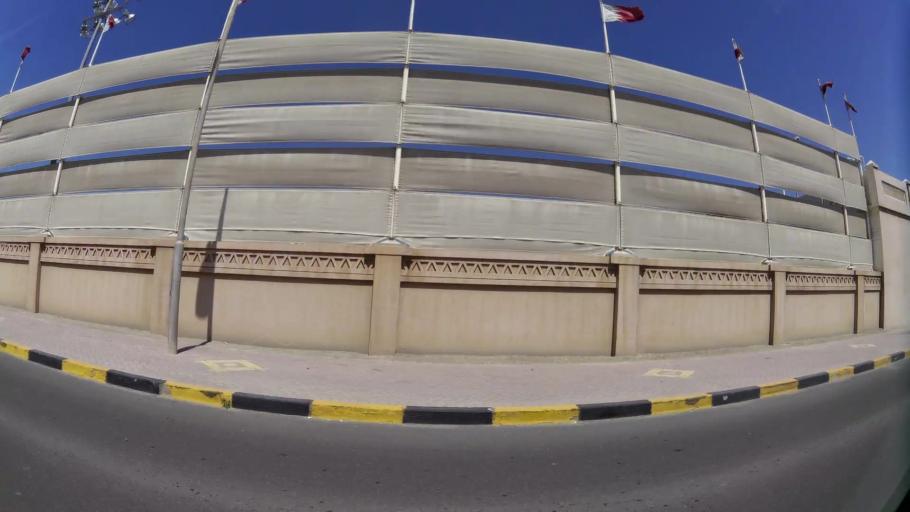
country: BH
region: Manama
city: Manama
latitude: 26.2206
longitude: 50.5930
